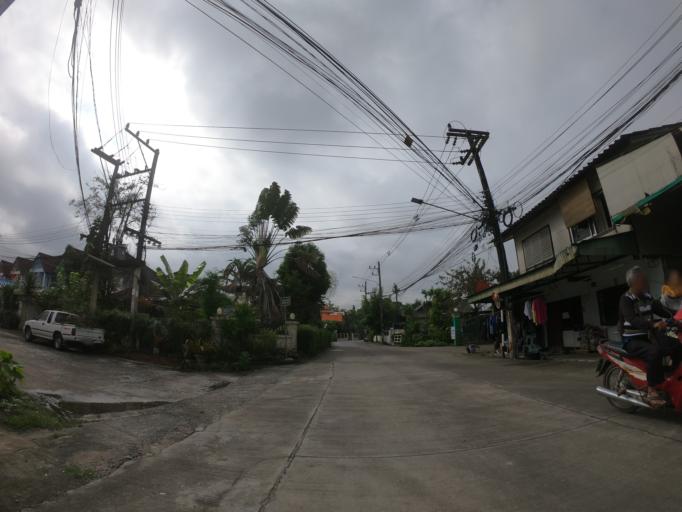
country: TH
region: Chiang Mai
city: Chiang Mai
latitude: 18.8164
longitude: 99.0069
